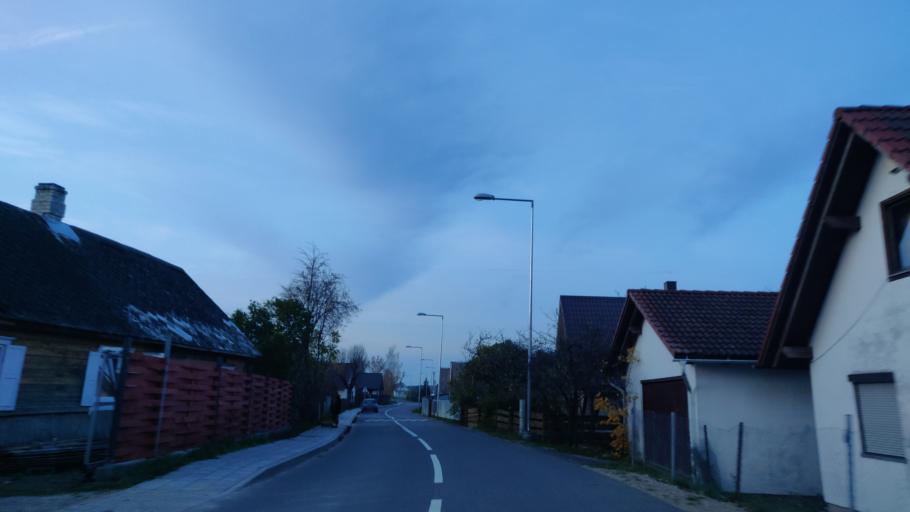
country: LT
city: Lentvaris
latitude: 54.5864
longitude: 25.0513
